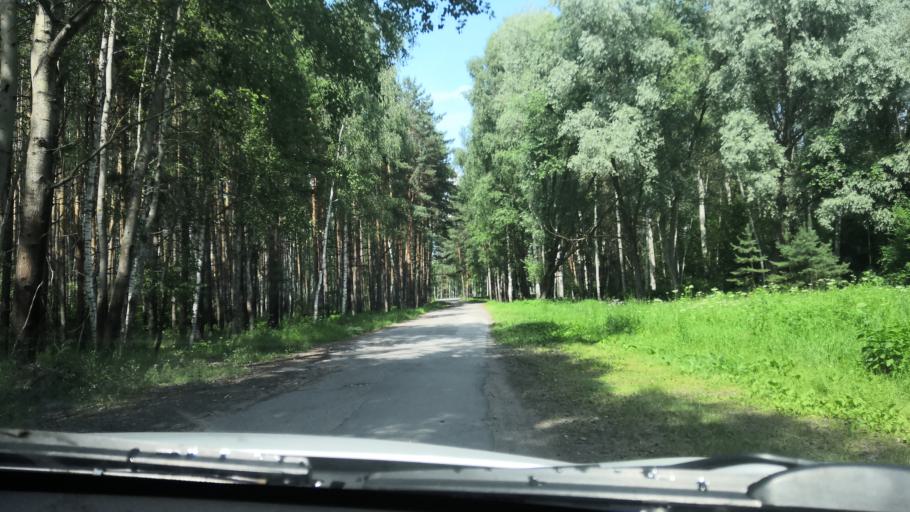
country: RU
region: Rjazan
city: Murmino
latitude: 54.5386
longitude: 40.1722
